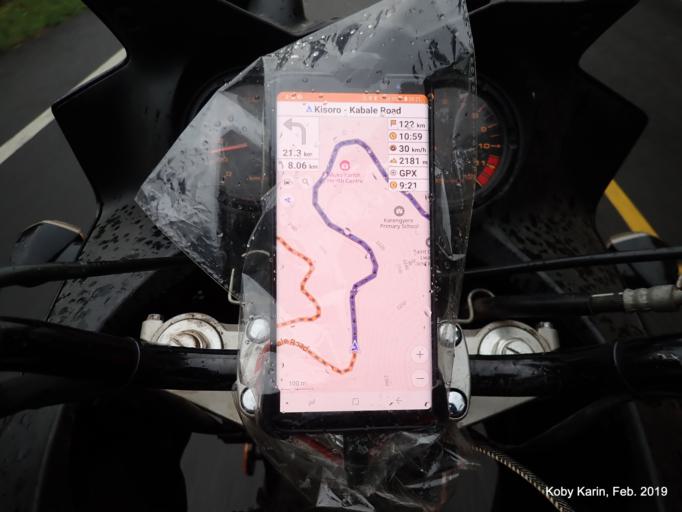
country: UG
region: Western Region
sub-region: Kisoro District
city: Kisoro
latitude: -1.2064
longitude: 29.8026
